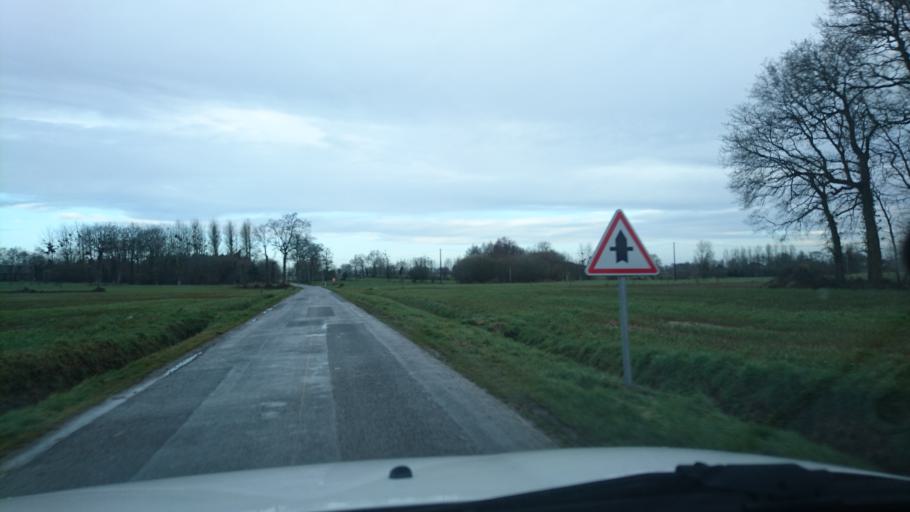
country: FR
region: Brittany
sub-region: Departement d'Ille-et-Vilaine
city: Antrain
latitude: 48.4874
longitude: -1.5191
